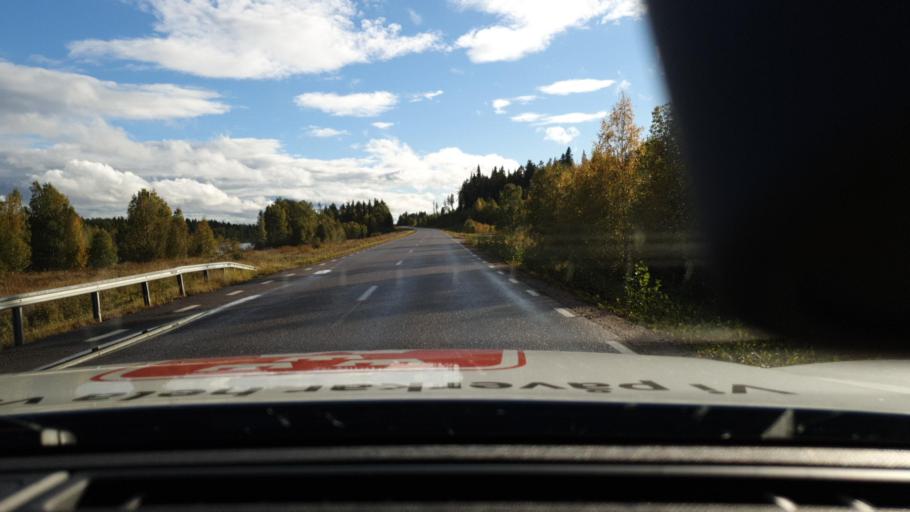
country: SE
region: Norrbotten
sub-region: Overkalix Kommun
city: OEverkalix
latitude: 66.7744
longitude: 22.6938
